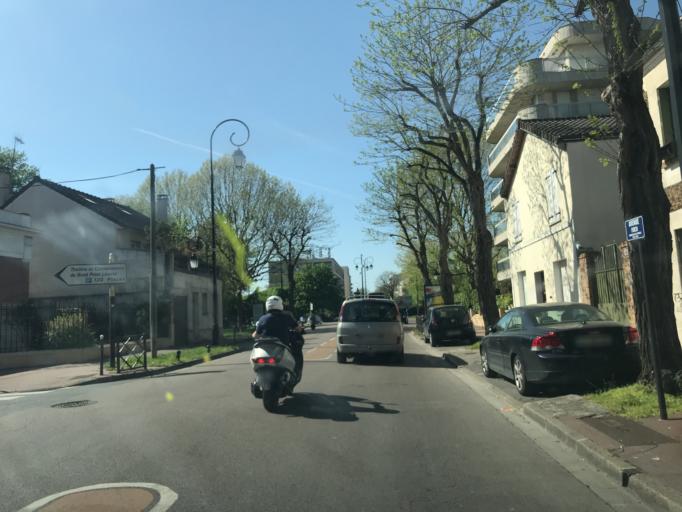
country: FR
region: Ile-de-France
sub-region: Departement du Val-de-Marne
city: Saint-Maur-des-Fosses
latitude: 48.8017
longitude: 2.4935
